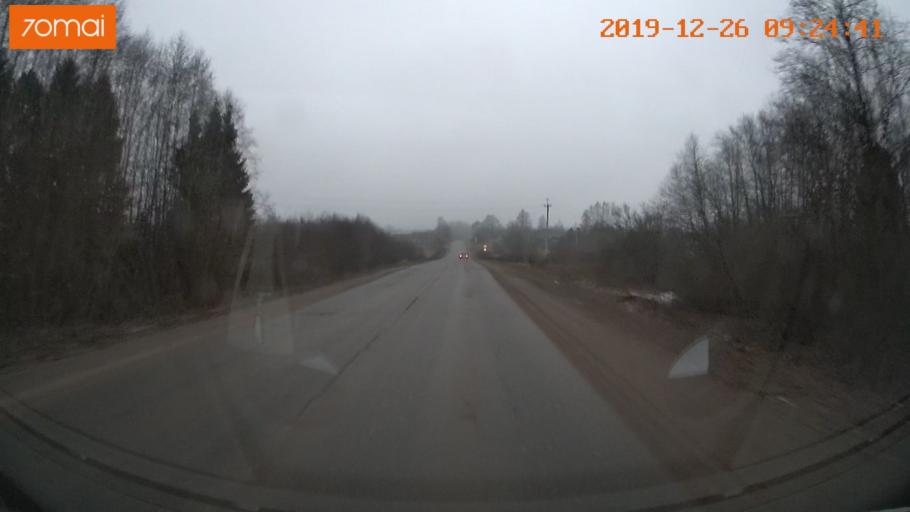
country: RU
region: Vologda
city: Gryazovets
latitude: 59.0036
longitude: 40.1963
